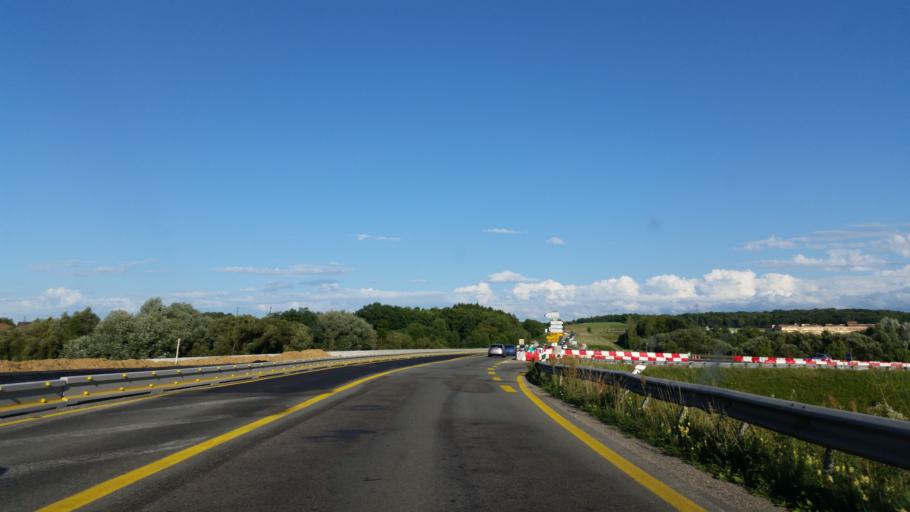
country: FR
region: Franche-Comte
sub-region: Territoire de Belfort
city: Andelnans
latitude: 47.5849
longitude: 6.8588
